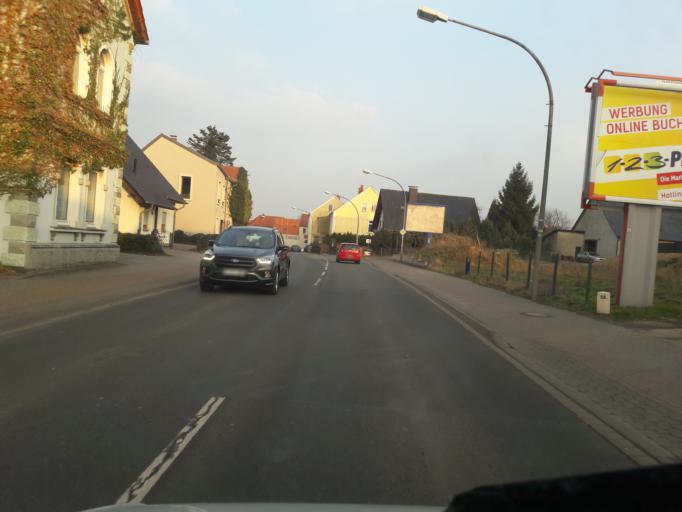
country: DE
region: North Rhine-Westphalia
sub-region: Regierungsbezirk Detmold
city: Huellhorst
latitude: 52.3096
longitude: 8.6536
